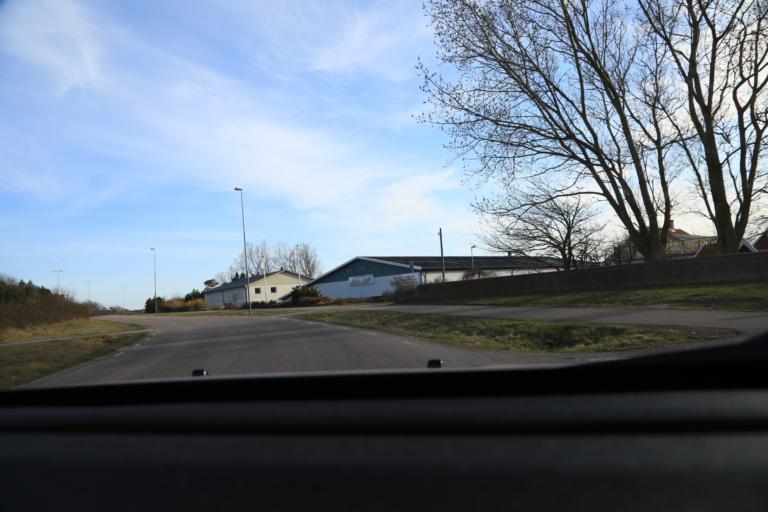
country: SE
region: Halland
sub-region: Varbergs Kommun
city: Traslovslage
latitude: 57.0798
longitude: 12.2786
